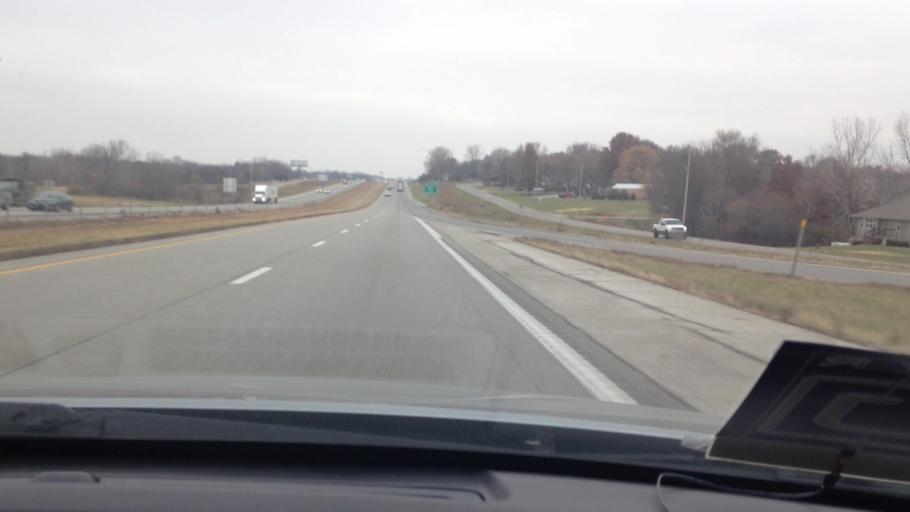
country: US
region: Missouri
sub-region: Cass County
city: Peculiar
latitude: 38.7251
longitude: -94.4567
